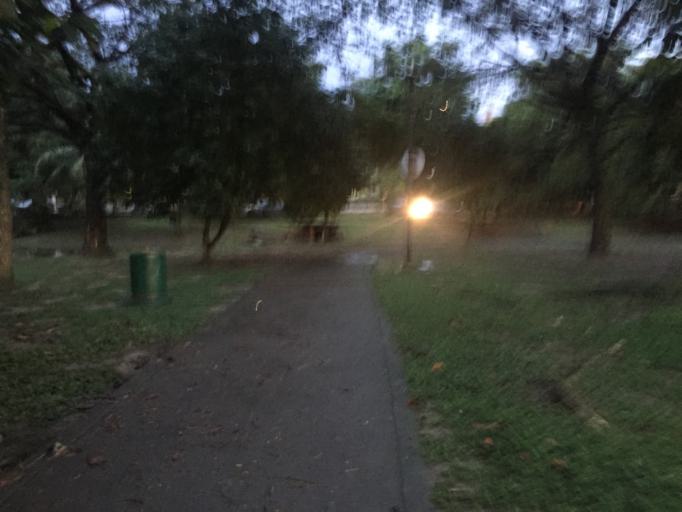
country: MY
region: Selangor
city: Klang
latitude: 2.9880
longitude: 101.4373
